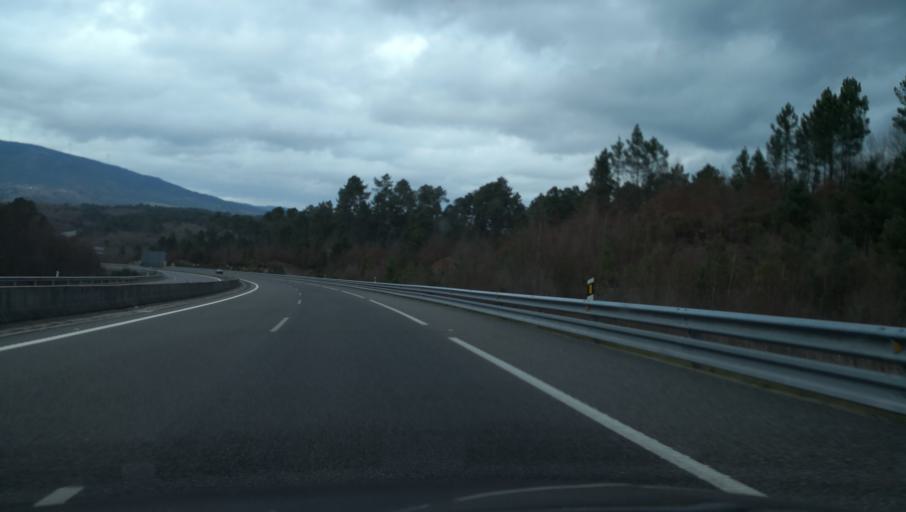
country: ES
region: Galicia
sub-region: Provincia de Ourense
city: Cea
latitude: 42.4571
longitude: -8.0232
